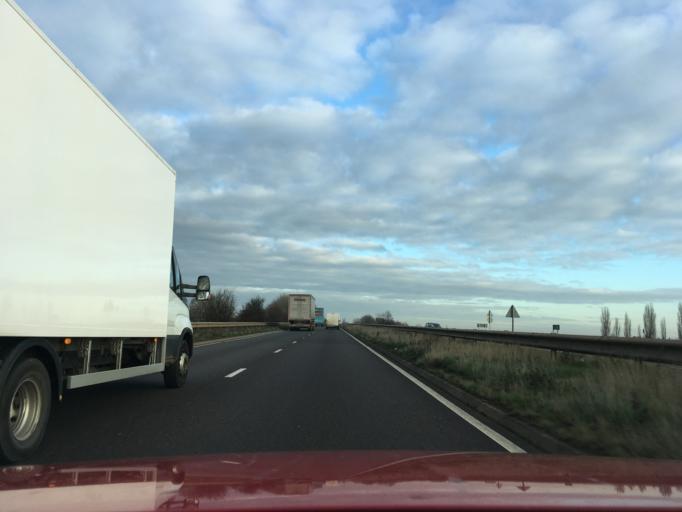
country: GB
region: England
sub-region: Staffordshire
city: Whittington
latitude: 52.6877
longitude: -1.7910
